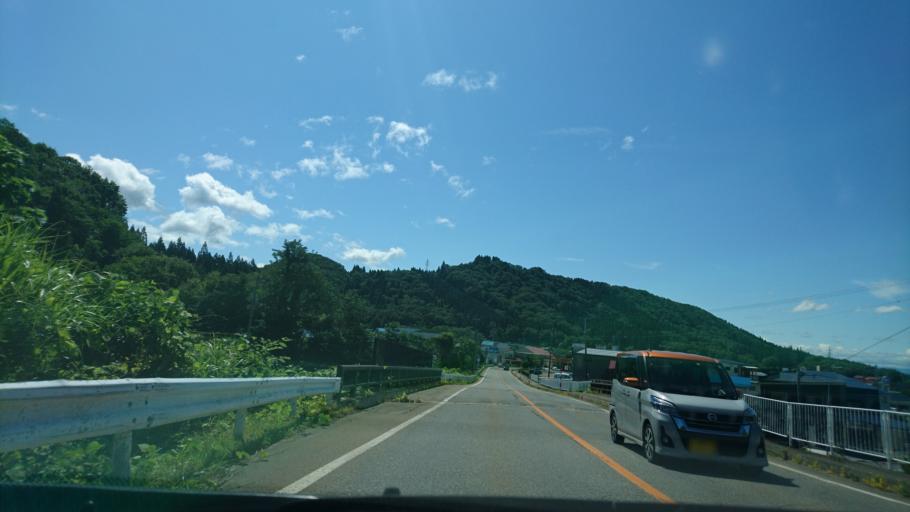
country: JP
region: Akita
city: Kakunodatemachi
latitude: 39.5966
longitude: 140.5755
